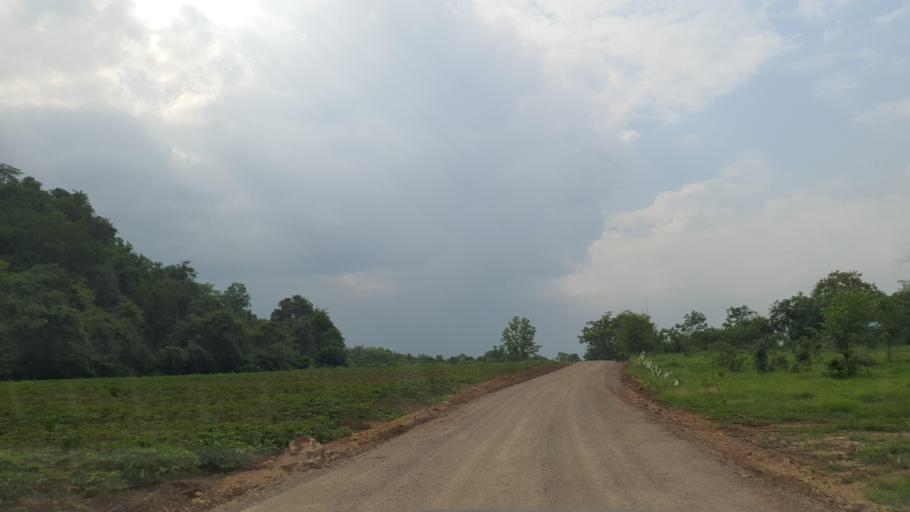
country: TH
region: Sukhothai
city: Thung Saliam
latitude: 17.2601
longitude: 99.5386
